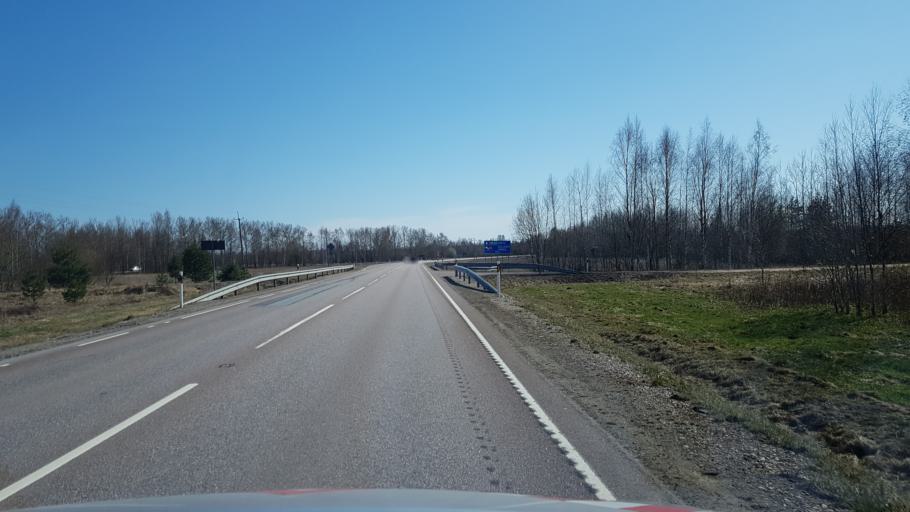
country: EE
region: Jogevamaa
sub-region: Mustvee linn
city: Mustvee
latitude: 58.7962
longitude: 26.9430
